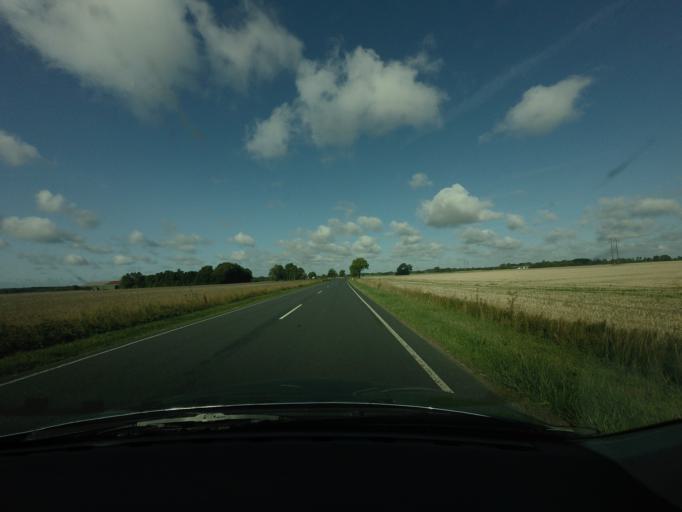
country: DK
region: Zealand
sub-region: Stevns Kommune
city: Harlev
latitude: 55.2781
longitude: 12.2467
